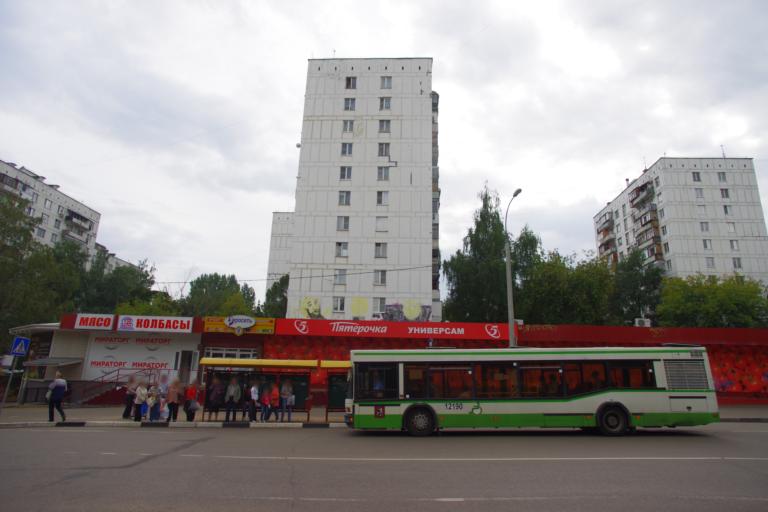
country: RU
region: Moskovskaya
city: Krasnogorsk
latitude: 55.8176
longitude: 37.3103
